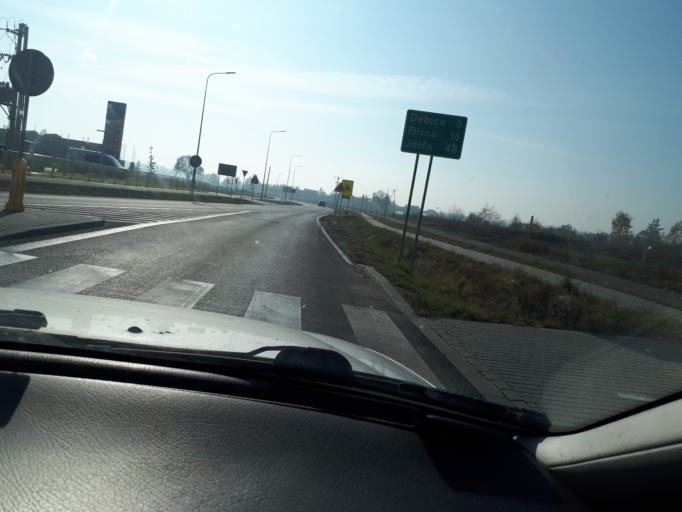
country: PL
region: Subcarpathian Voivodeship
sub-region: Powiat debicki
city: Zyrakow
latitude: 50.0759
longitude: 21.3825
